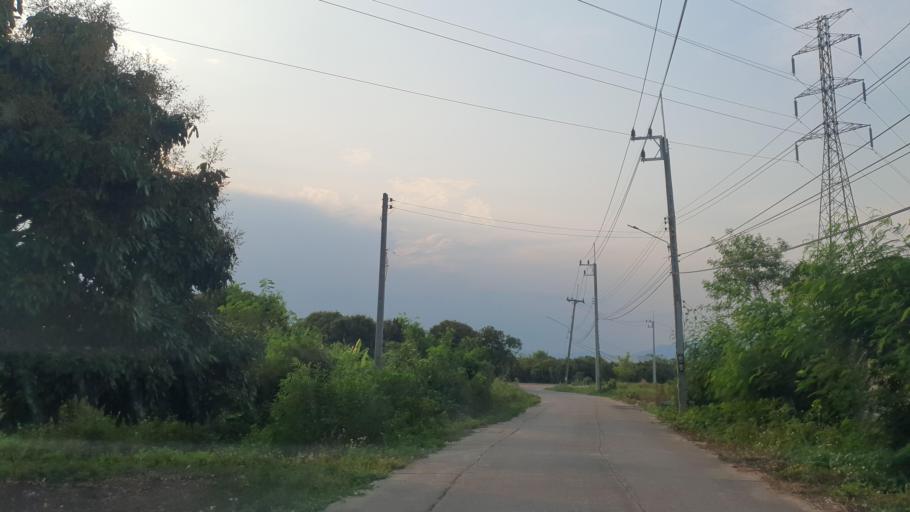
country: TH
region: Chiang Mai
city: Hang Dong
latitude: 18.6572
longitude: 98.9359
